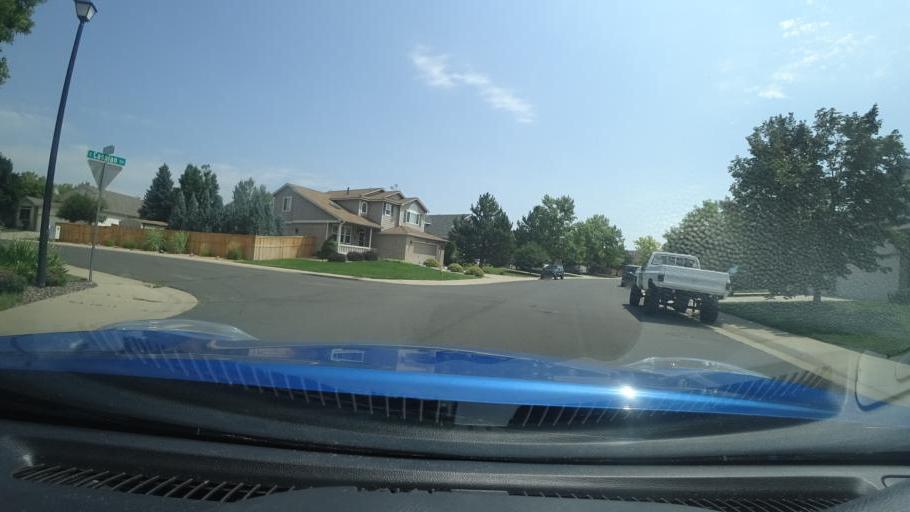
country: US
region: Colorado
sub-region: Adams County
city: Aurora
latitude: 39.6777
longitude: -104.7570
